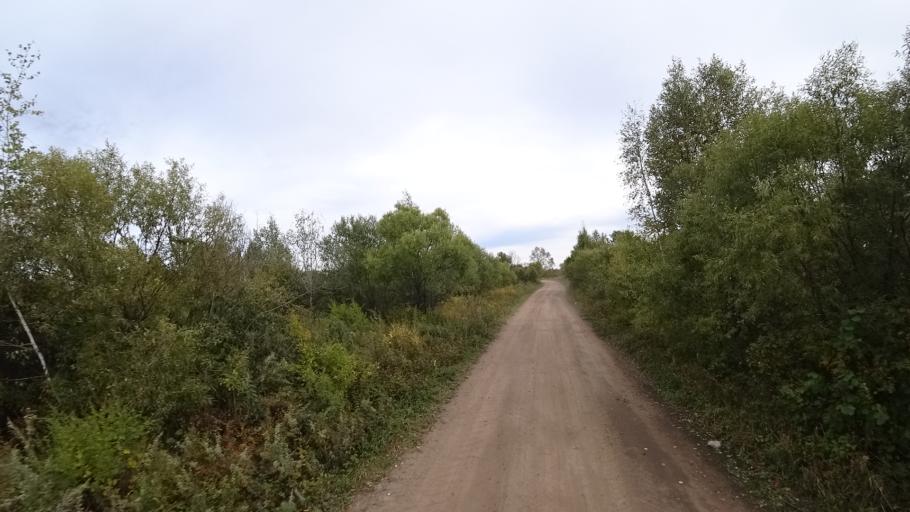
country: RU
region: Amur
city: Arkhara
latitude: 49.3415
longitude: 130.1041
